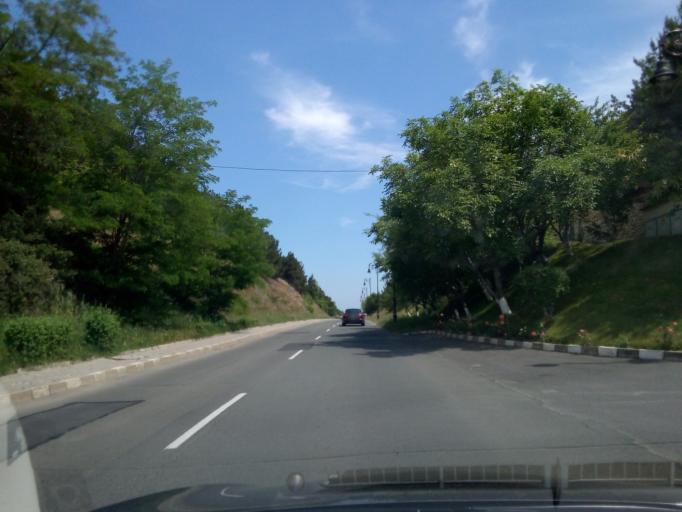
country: BG
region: Burgas
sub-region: Obshtina Nesebur
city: Sveti Vlas
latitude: 42.7095
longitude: 27.7736
